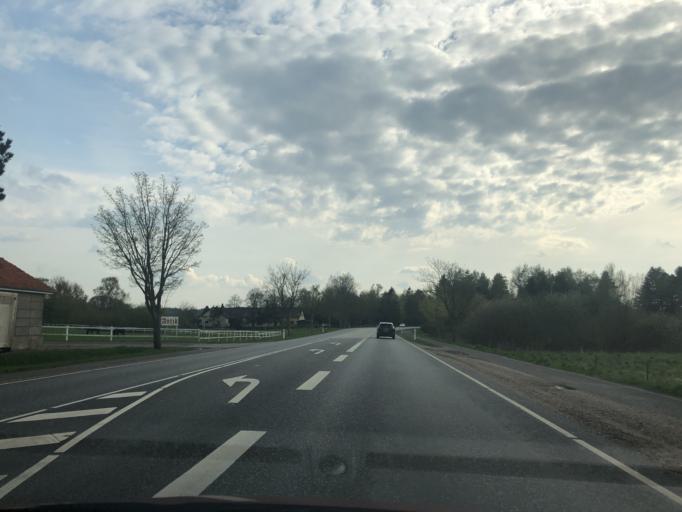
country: DK
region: Zealand
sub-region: Lejre Kommune
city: Osted
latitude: 55.5461
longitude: 11.9414
